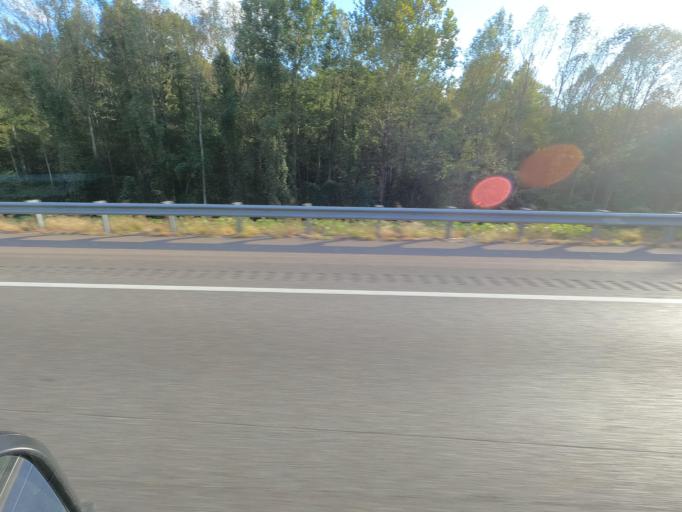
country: US
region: Tennessee
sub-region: Decatur County
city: Parsons
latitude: 35.8173
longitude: -88.2466
